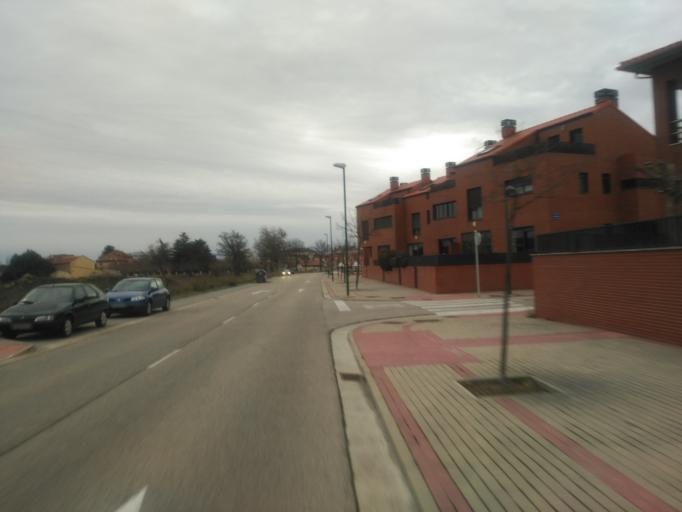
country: ES
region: Castille and Leon
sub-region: Provincia de Burgos
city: Villagonzalo-Pedernales
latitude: 42.3413
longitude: -3.7360
